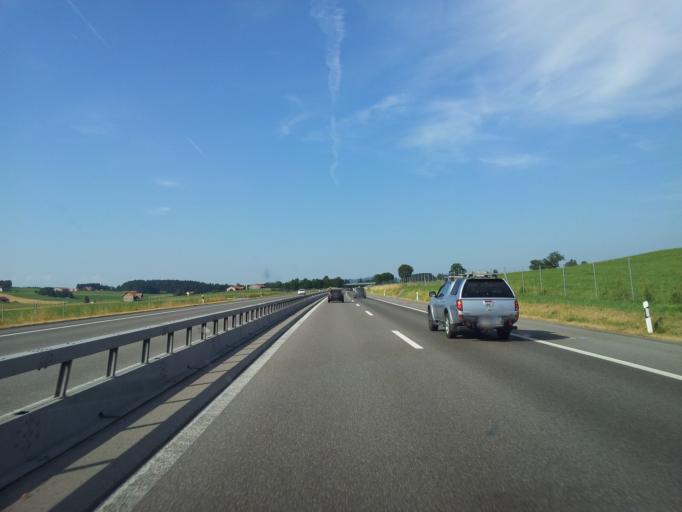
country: CH
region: Fribourg
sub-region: Gruyere District
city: Sales
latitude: 46.5878
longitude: 6.9309
